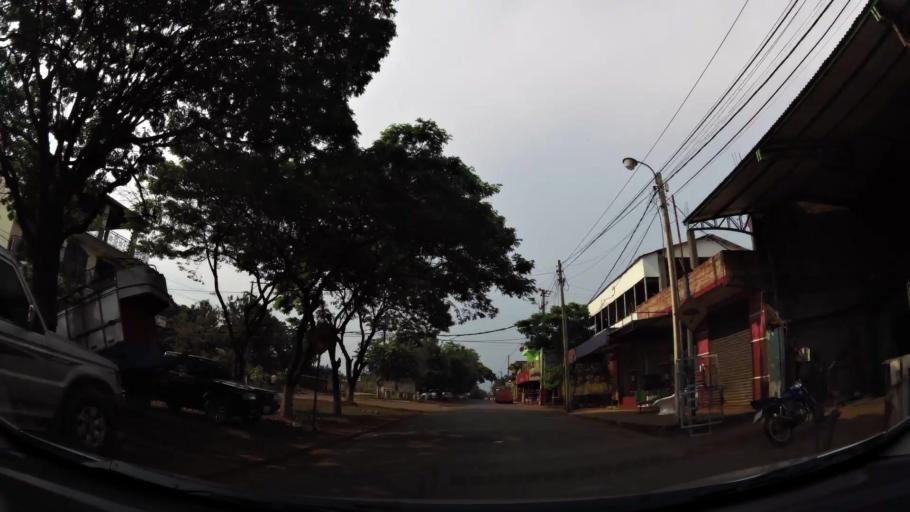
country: PY
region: Alto Parana
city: Ciudad del Este
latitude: -25.4879
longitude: -54.6469
